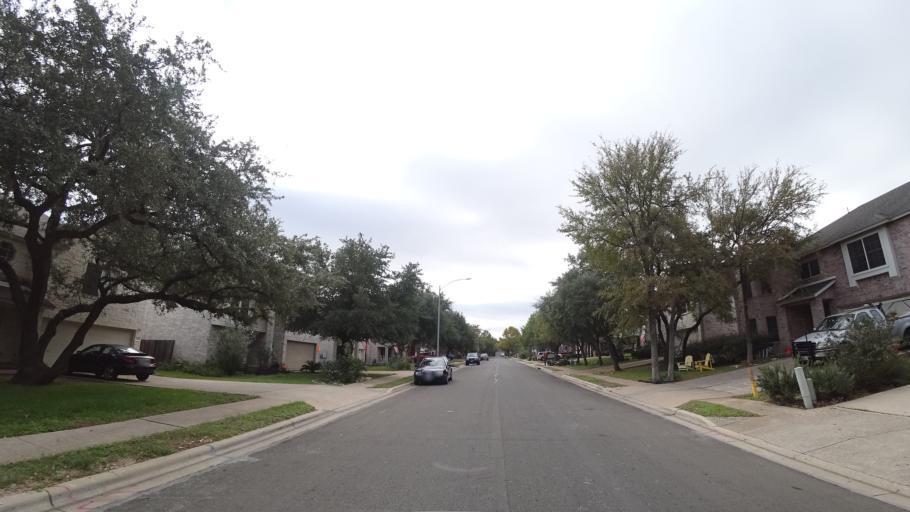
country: US
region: Texas
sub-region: Travis County
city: Manchaca
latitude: 30.1566
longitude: -97.8398
